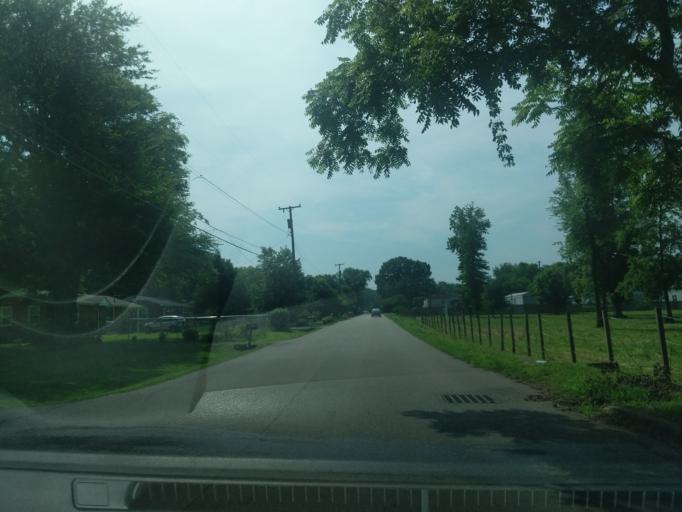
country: US
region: Tennessee
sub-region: Davidson County
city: Lakewood
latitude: 36.2735
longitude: -86.6705
